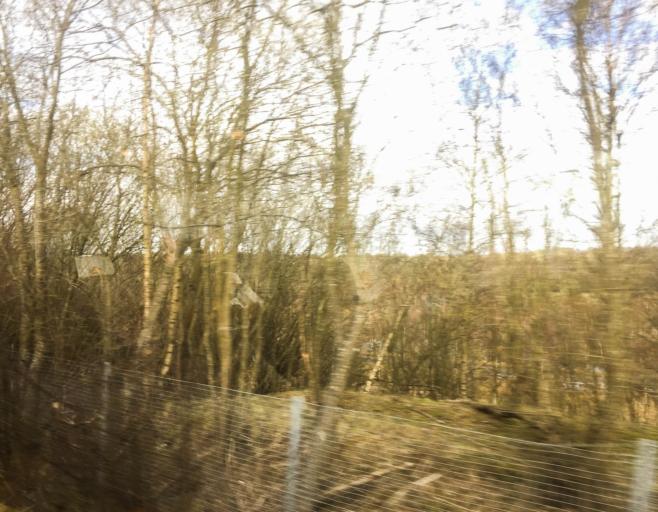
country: GB
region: Scotland
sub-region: North Lanarkshire
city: Newarthill
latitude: 55.7850
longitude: -3.9474
